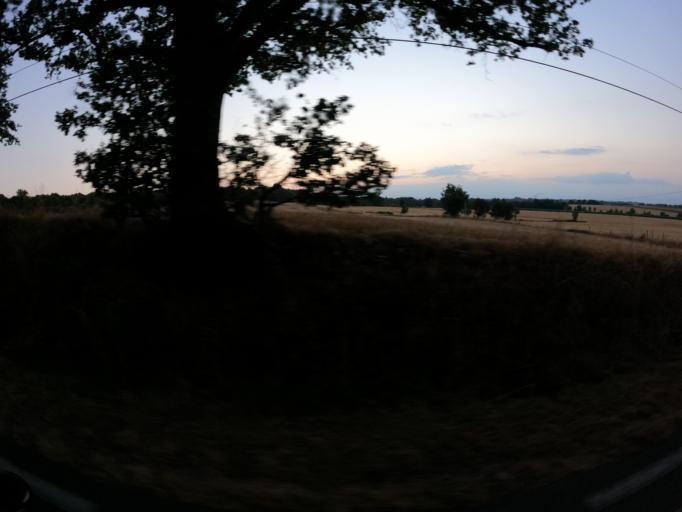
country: FR
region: Pays de la Loire
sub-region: Departement de Maine-et-Loire
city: Cande
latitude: 47.6056
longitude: -0.9903
